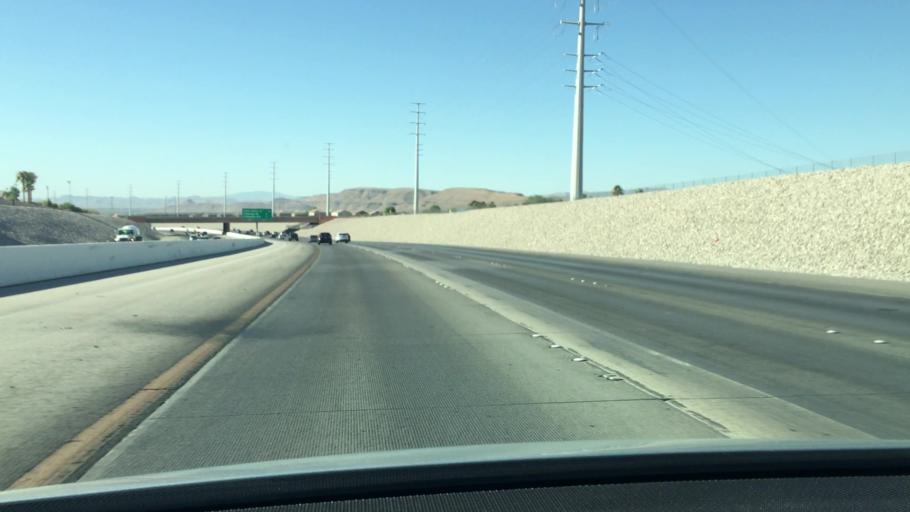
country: US
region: Nevada
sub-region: Clark County
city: Summerlin South
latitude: 36.1332
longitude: -115.3362
